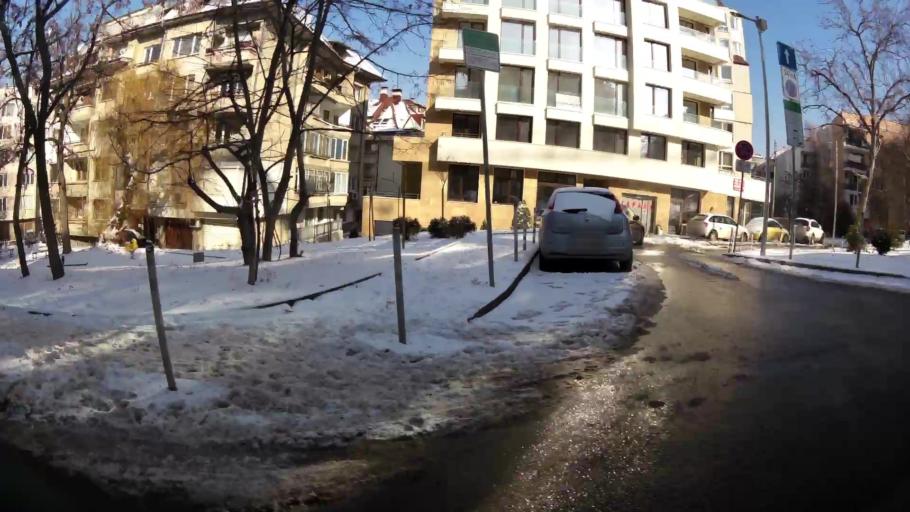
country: BG
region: Sofia-Capital
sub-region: Stolichna Obshtina
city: Sofia
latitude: 42.6730
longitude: 23.3136
